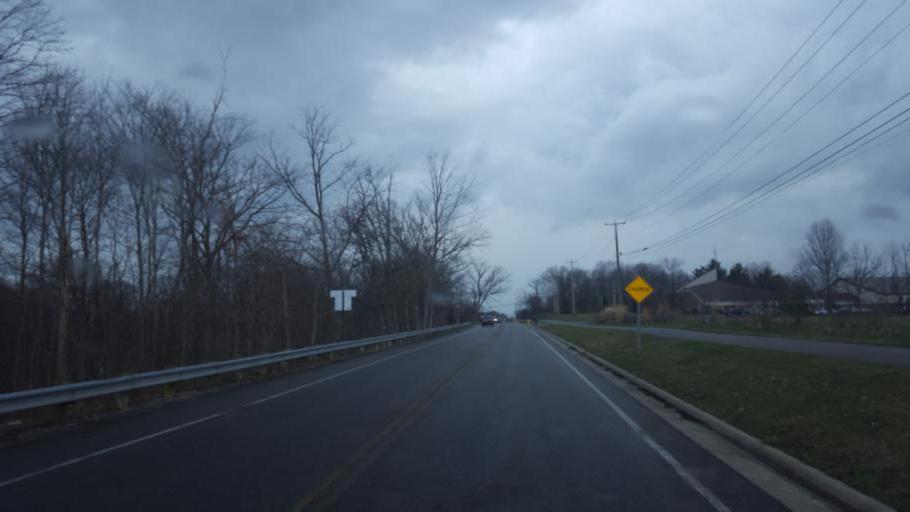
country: US
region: Ohio
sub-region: Delaware County
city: Lewis Center
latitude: 40.1729
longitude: -82.9657
